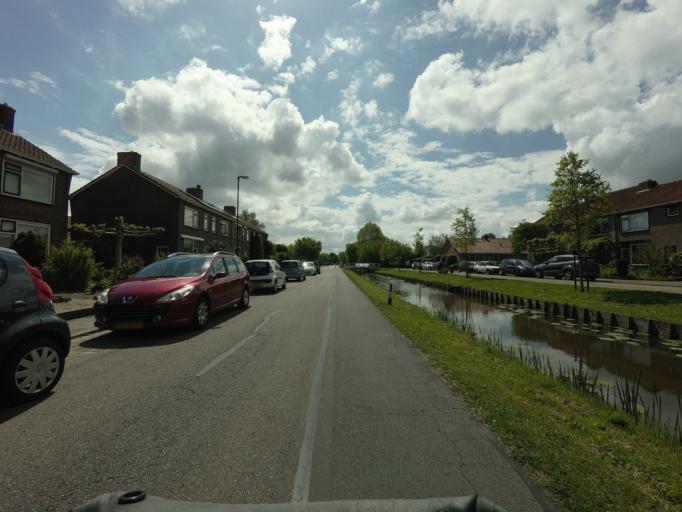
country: NL
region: South Holland
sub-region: Gemeente Gorinchem
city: Gorinchem
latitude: 51.8761
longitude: 4.9472
